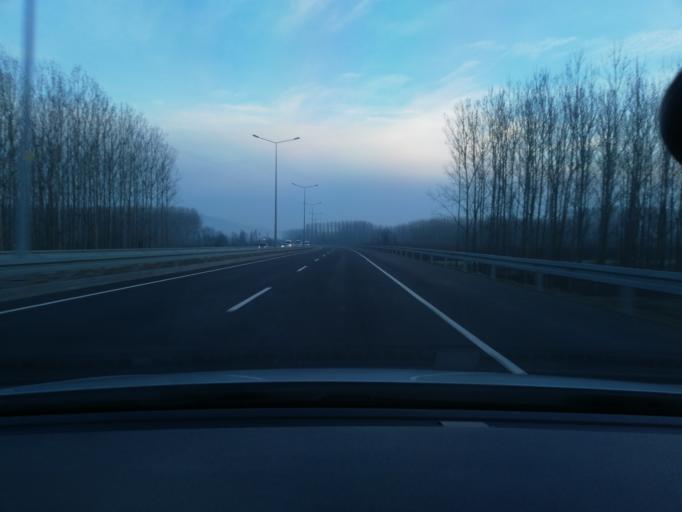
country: TR
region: Duzce
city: Duzce
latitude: 40.8086
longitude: 31.1689
